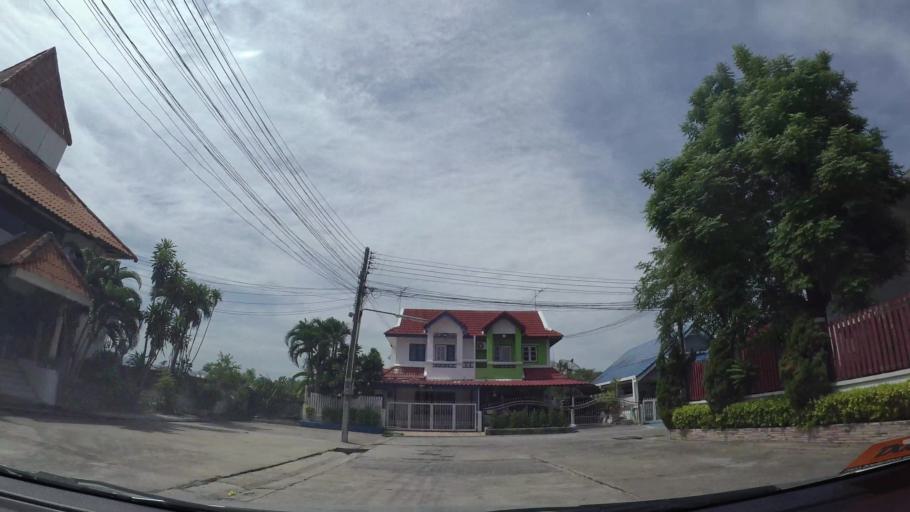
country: TH
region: Chon Buri
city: Chon Buri
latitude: 13.3229
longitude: 100.9501
